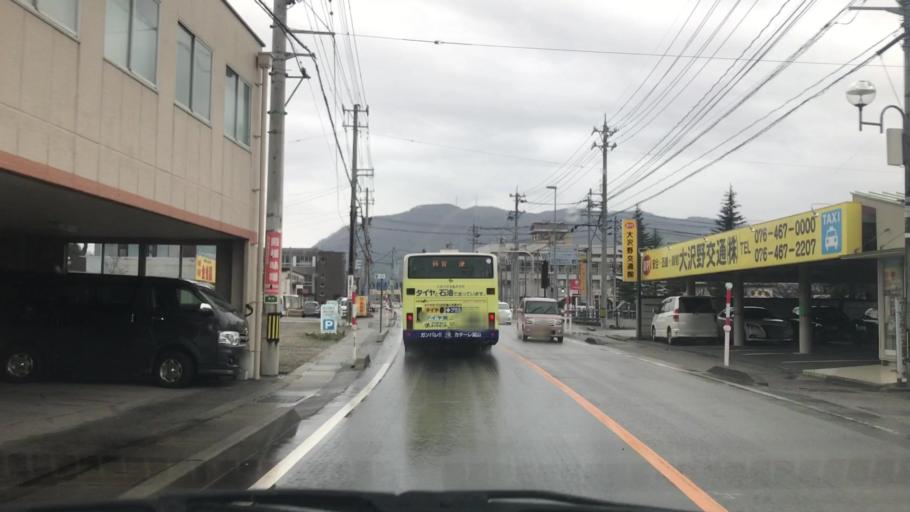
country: JP
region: Toyama
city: Yatsuomachi-higashikumisaka
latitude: 36.5803
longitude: 137.2065
